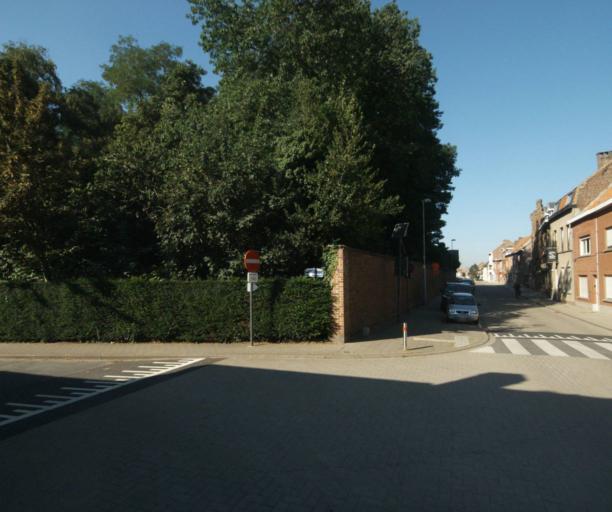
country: BE
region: Flanders
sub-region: Provincie West-Vlaanderen
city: Wervik
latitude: 50.7787
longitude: 3.0379
